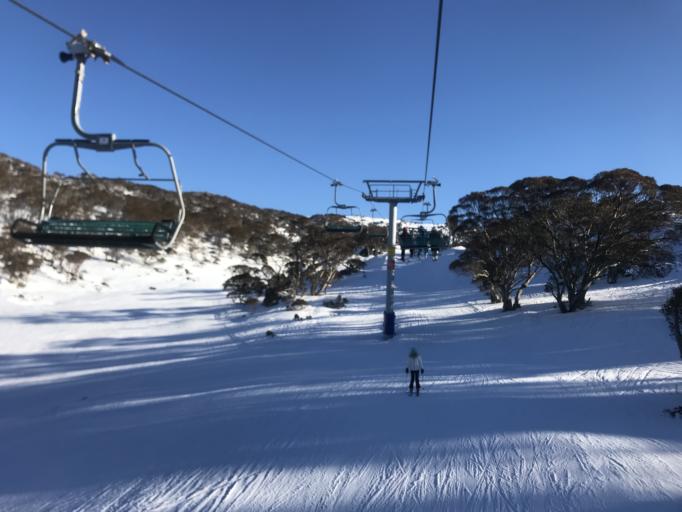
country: AU
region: New South Wales
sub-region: Snowy River
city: Jindabyne
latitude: -36.3875
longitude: 148.3990
